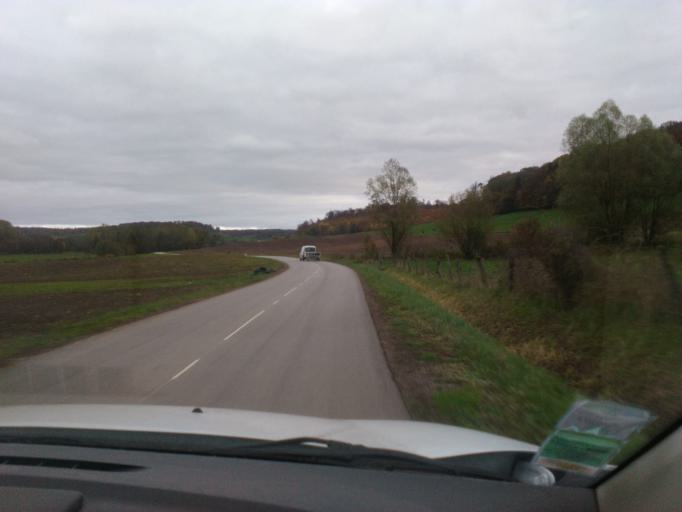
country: FR
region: Lorraine
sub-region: Departement des Vosges
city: Mirecourt
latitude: 48.2747
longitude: 6.2378
